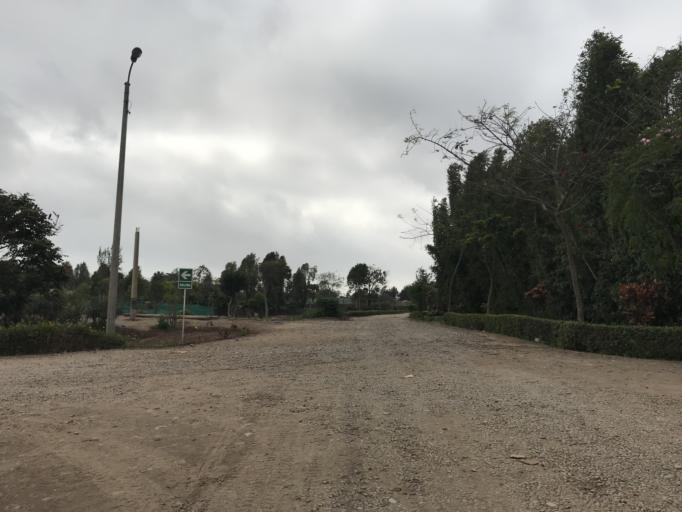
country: PE
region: Callao
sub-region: Callao
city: Callao
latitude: -12.0662
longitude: -77.0843
